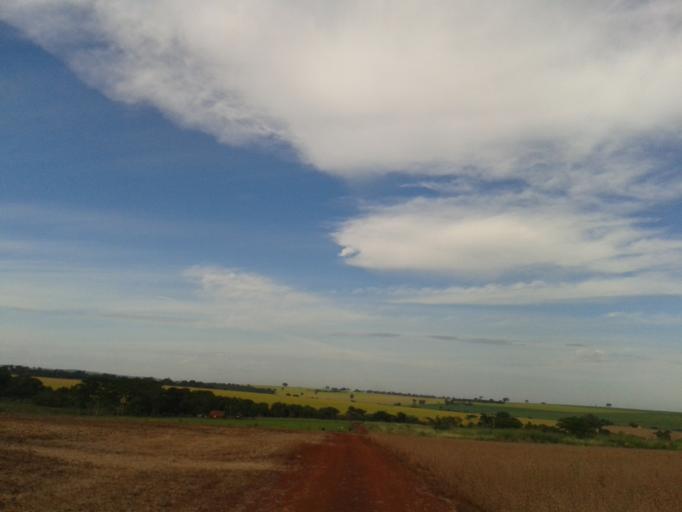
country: BR
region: Minas Gerais
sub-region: Capinopolis
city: Capinopolis
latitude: -18.6524
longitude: -49.6923
